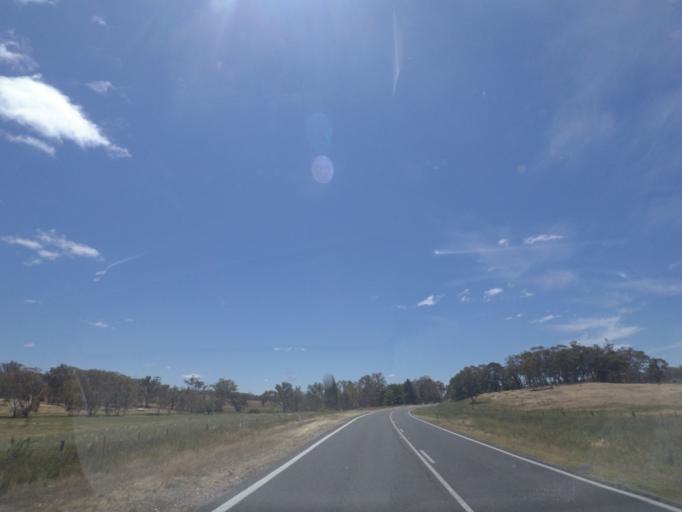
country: AU
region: Victoria
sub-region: Mount Alexander
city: Castlemaine
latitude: -37.1726
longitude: 144.1462
